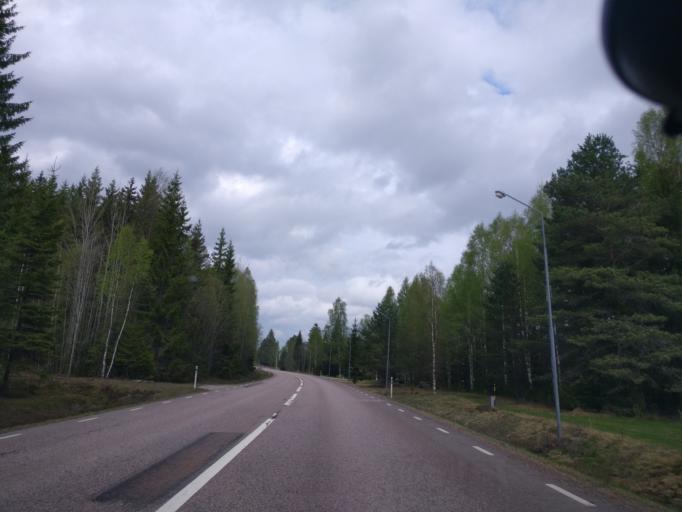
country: SE
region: Vaermland
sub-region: Hagfors Kommun
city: Ekshaerad
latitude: 60.1426
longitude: 13.5249
